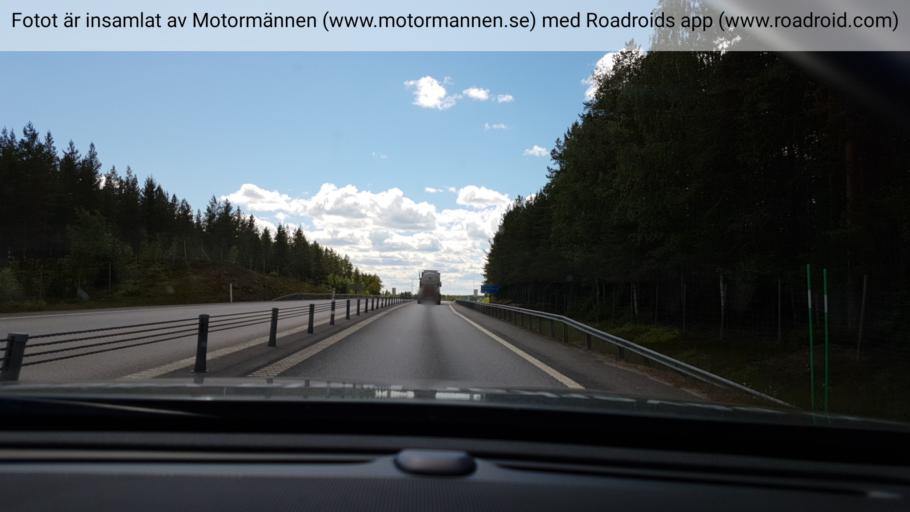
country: SE
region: Vaesterbotten
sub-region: Umea Kommun
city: Saevar
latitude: 63.9025
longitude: 20.5739
